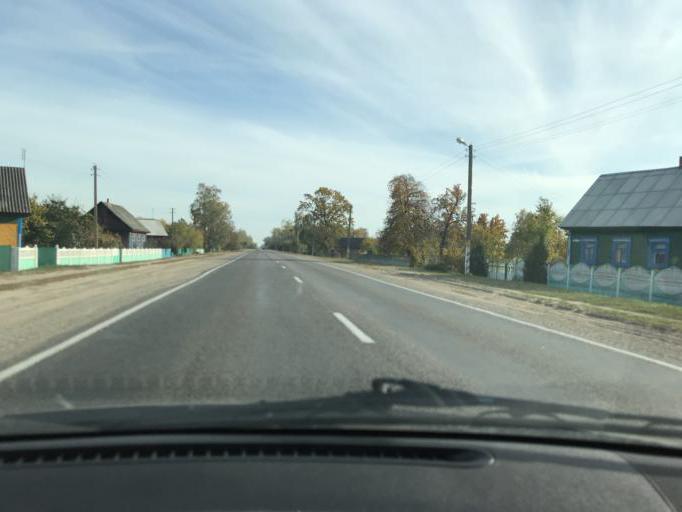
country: BY
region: Brest
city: Lahishyn
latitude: 52.2335
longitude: 26.0138
